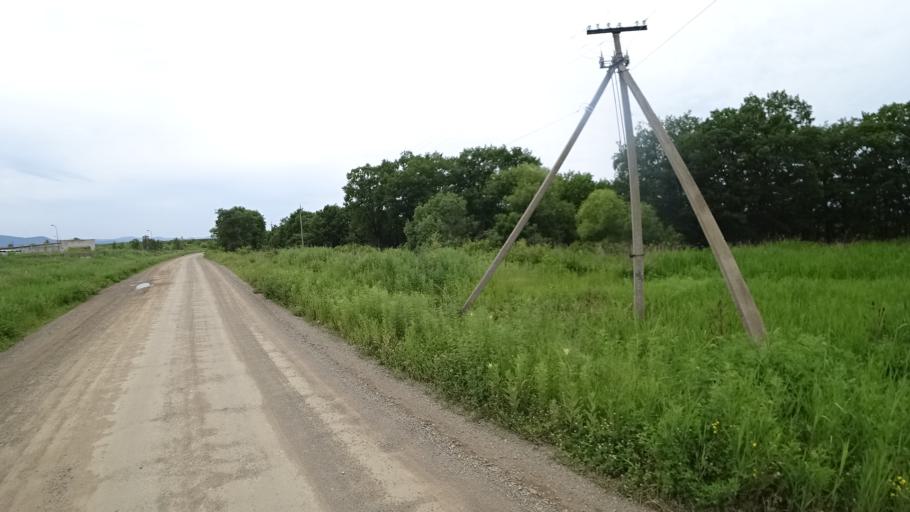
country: RU
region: Primorskiy
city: Arsen'yev
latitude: 44.2008
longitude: 133.3107
